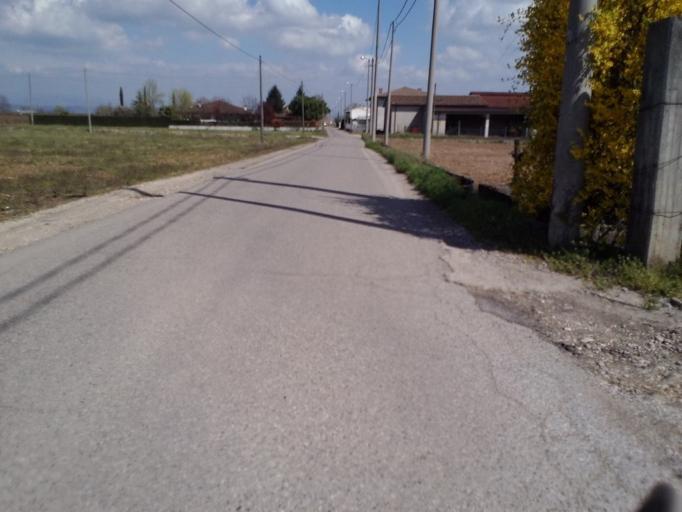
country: IT
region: Veneto
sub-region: Provincia di Verona
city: Dossobuono
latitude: 45.3970
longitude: 10.9279
